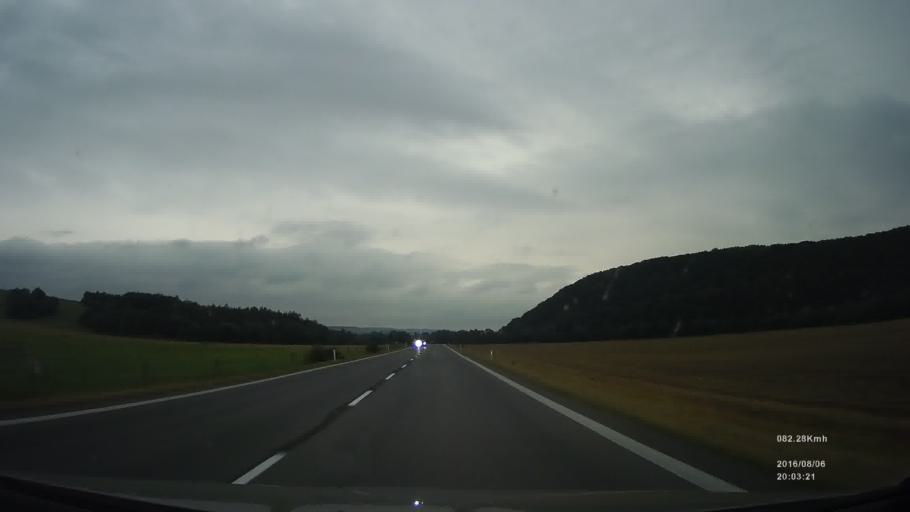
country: SK
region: Presovsky
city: Stropkov
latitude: 49.2501
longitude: 21.6082
